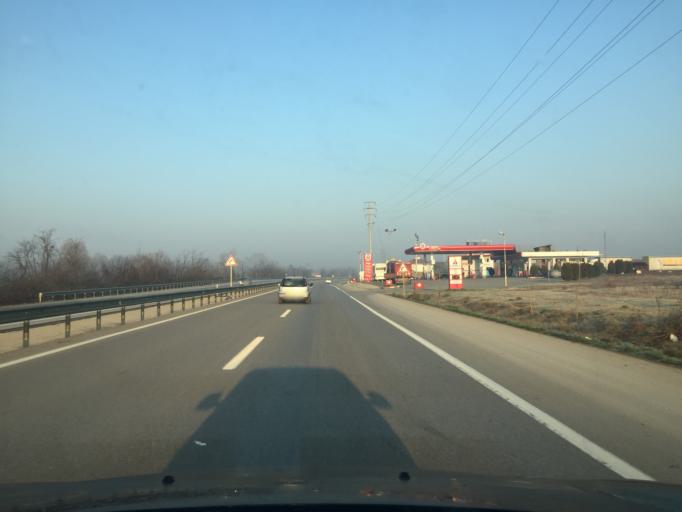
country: TR
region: Sakarya
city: Akyazi
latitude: 40.6781
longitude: 30.5809
